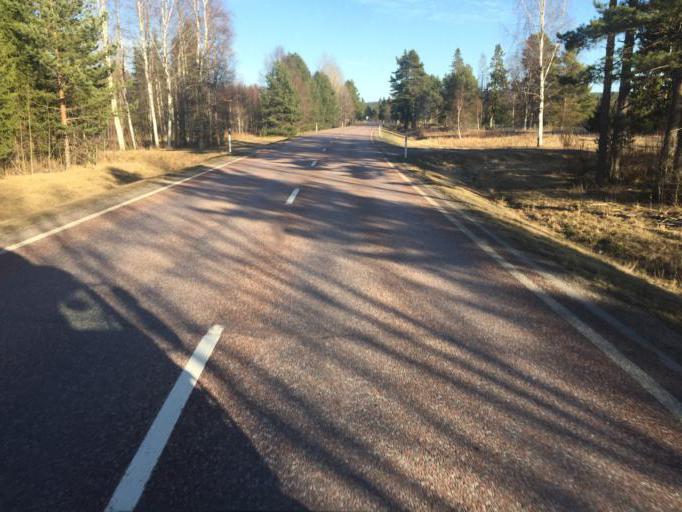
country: SE
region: Dalarna
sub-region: Vansbro Kommun
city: Jarna
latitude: 60.4696
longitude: 14.6506
